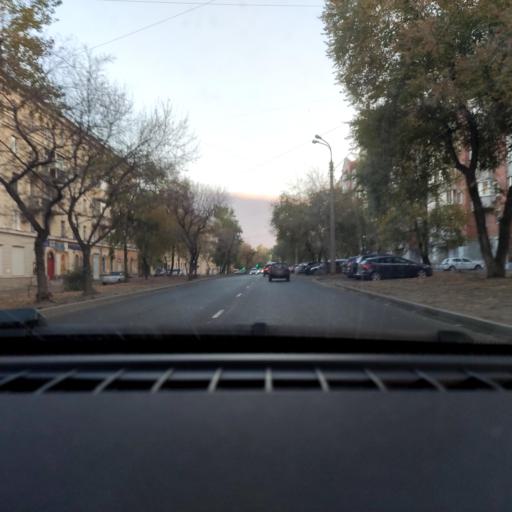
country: RU
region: Voronezj
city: Voronezh
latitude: 51.6367
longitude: 39.2381
